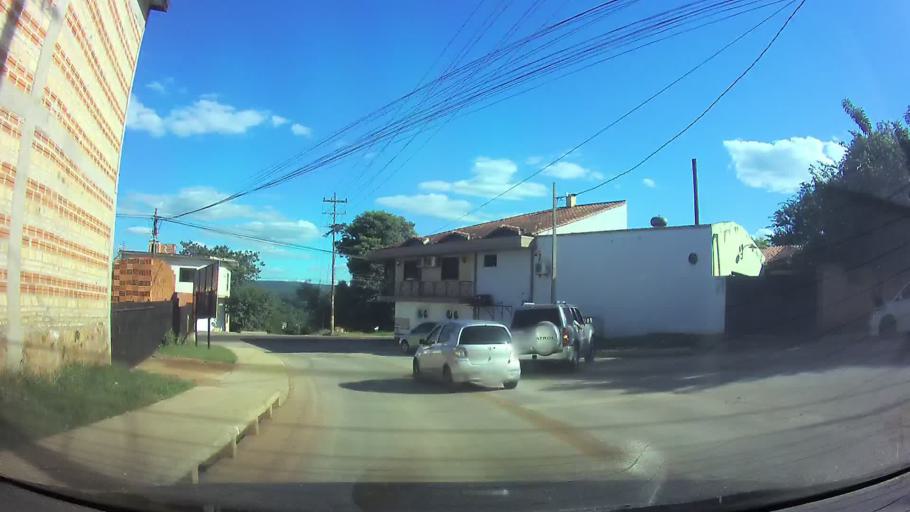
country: PY
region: Cordillera
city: Caacupe
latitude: -25.3743
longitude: -57.1379
